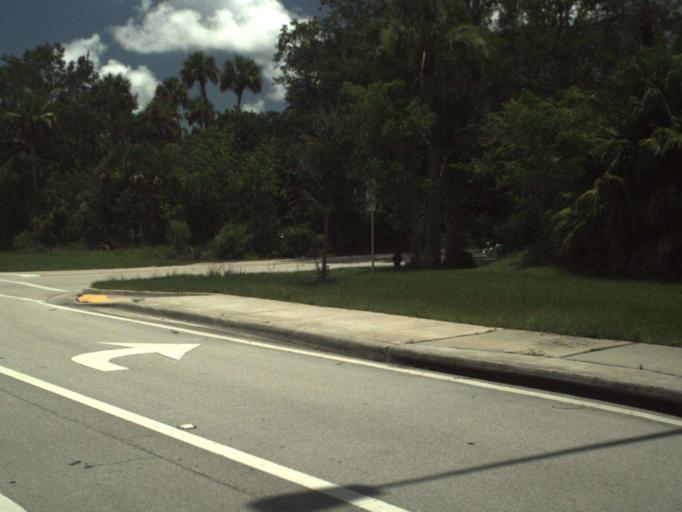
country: US
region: Florida
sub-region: Indian River County
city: West Vero Corridor
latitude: 27.6390
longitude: -80.4742
